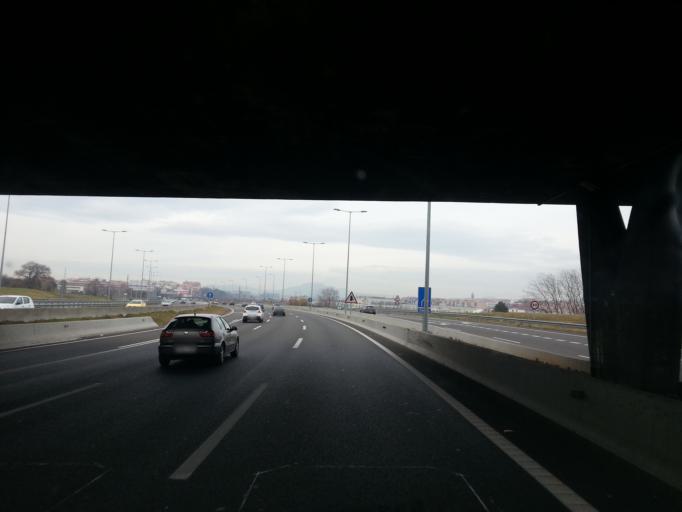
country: ES
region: Catalonia
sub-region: Provincia de Barcelona
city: Ripollet
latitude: 41.4876
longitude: 2.1595
